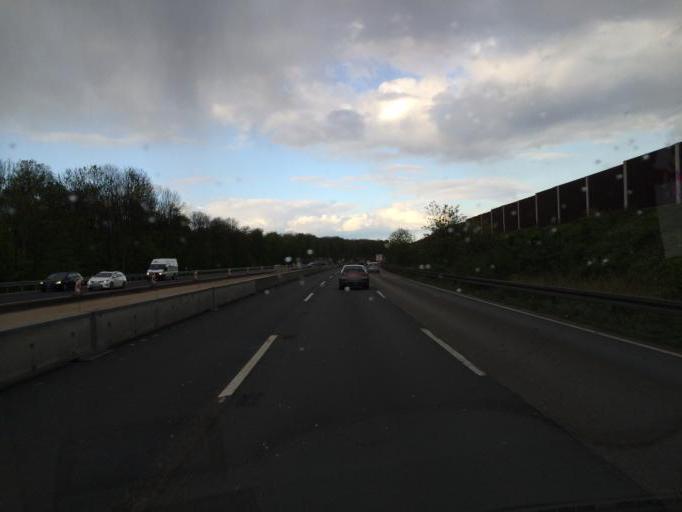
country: DE
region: North Rhine-Westphalia
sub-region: Regierungsbezirk Koln
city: Mengenich
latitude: 50.9845
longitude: 6.8562
